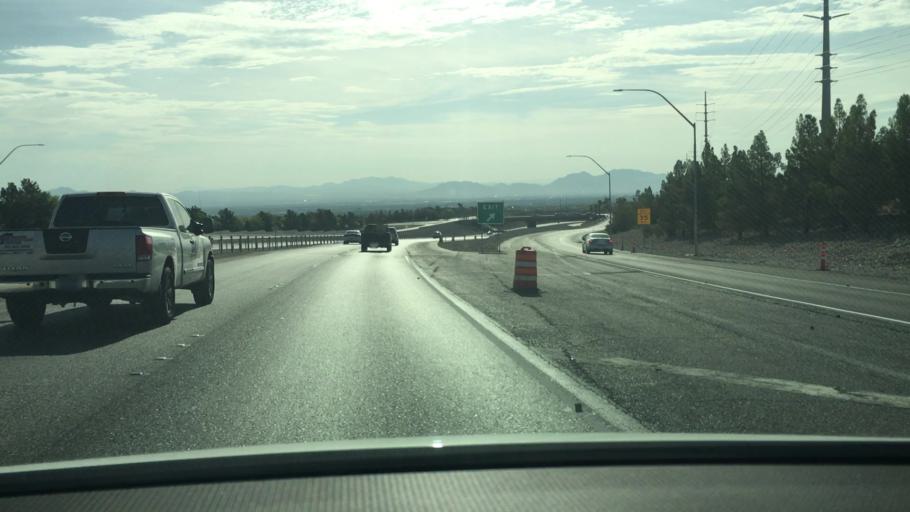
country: US
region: Nevada
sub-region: Clark County
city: Summerlin South
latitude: 36.1935
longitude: -115.3293
